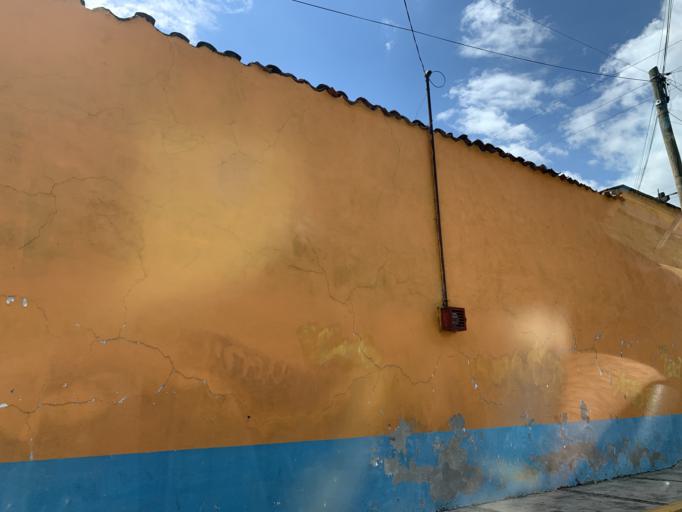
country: MX
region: Puebla
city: San Andres Cholula
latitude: 19.0456
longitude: -98.3001
